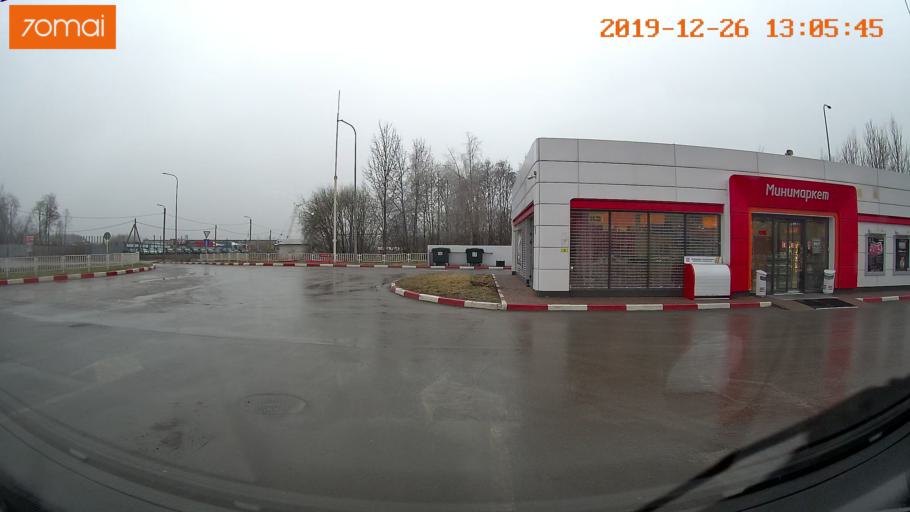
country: RU
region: Vologda
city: Cherepovets
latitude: 59.0782
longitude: 37.9135
